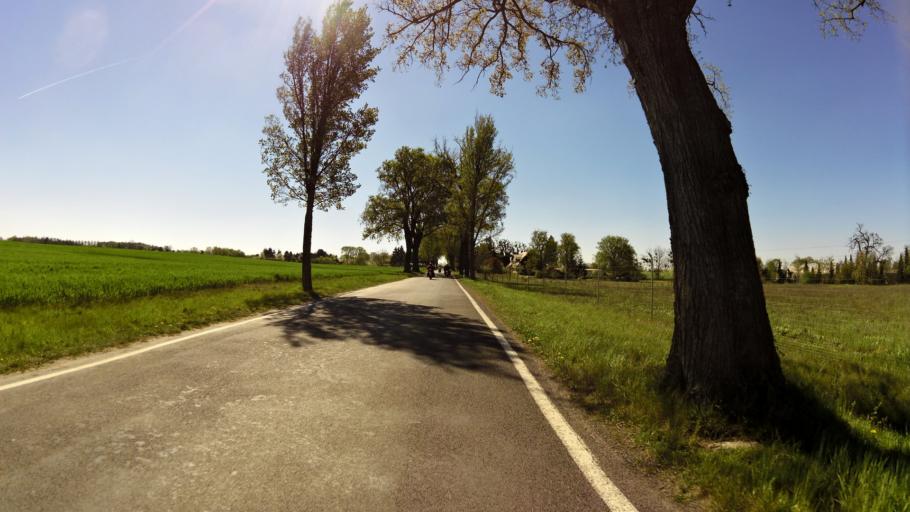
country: DE
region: Brandenburg
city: Werftpfuhl
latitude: 52.6444
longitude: 13.7925
